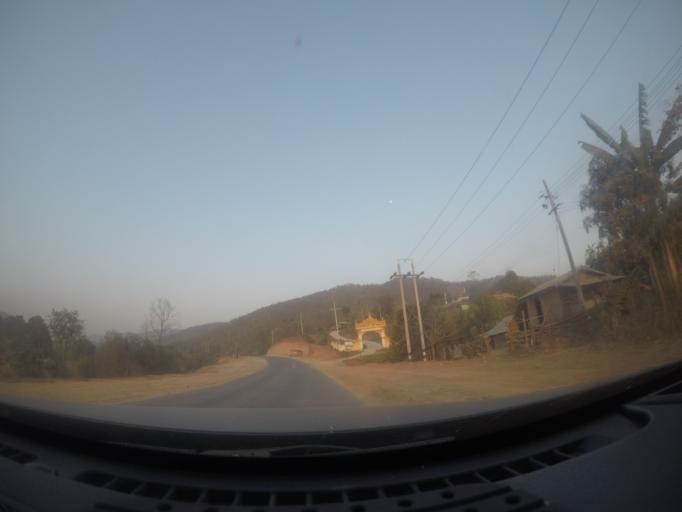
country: MM
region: Mandalay
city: Yamethin
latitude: 20.8062
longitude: 96.3766
